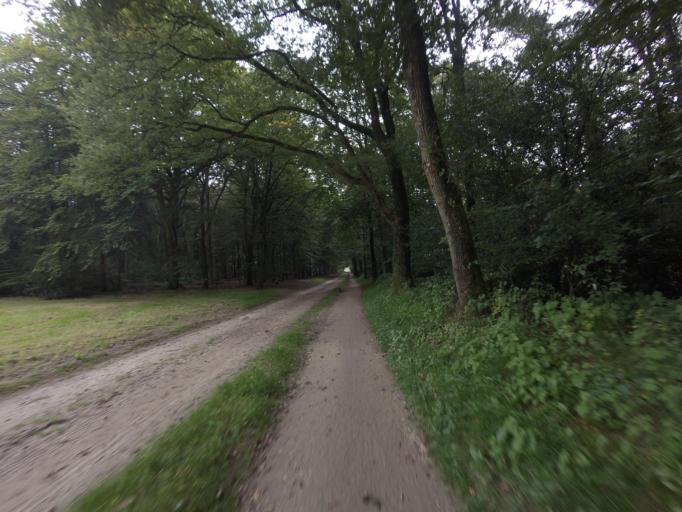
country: DE
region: Lower Saxony
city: Getelo
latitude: 52.4352
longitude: 6.8852
